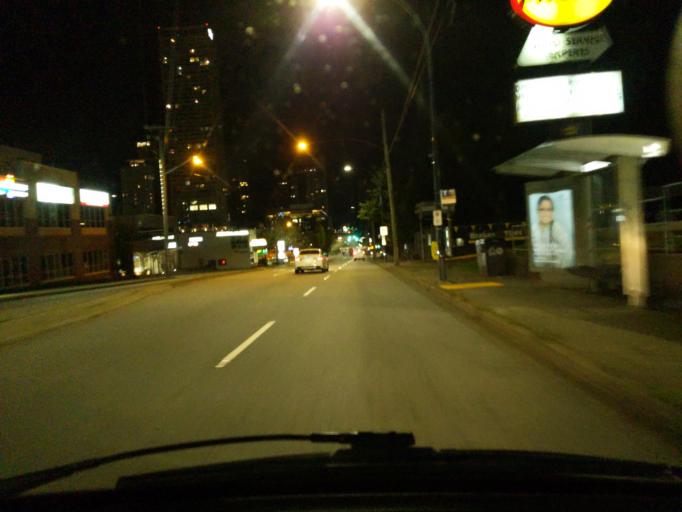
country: CA
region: British Columbia
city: New Westminster
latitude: 49.1917
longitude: -122.8425
